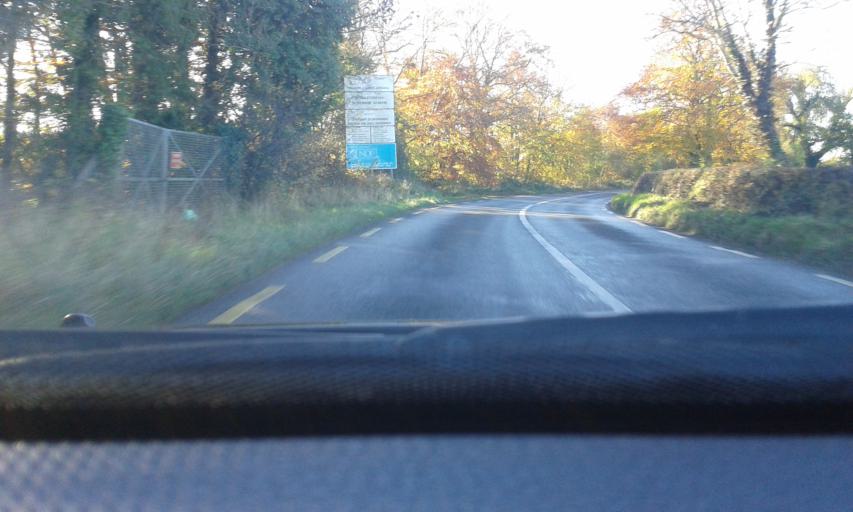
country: IE
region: Leinster
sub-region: Kildare
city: Monasterevin
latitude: 53.1583
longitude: -7.0412
